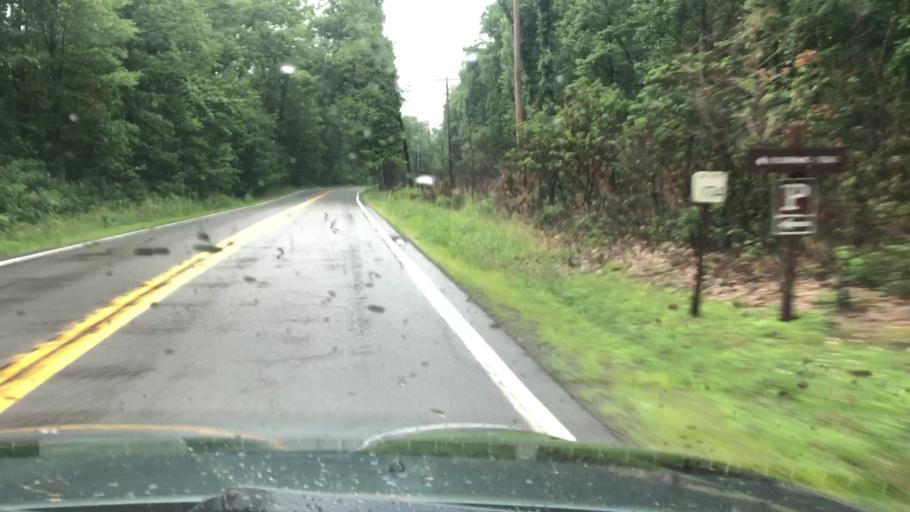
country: US
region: Pennsylvania
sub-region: Wayne County
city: Hawley
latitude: 41.3440
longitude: -75.2117
